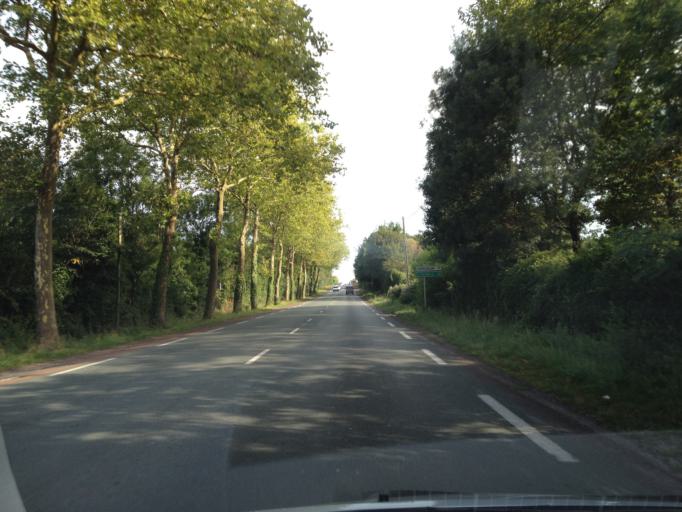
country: FR
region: Poitou-Charentes
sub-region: Departement de la Charente-Maritime
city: Rochefort
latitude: 45.9609
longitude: -0.9793
